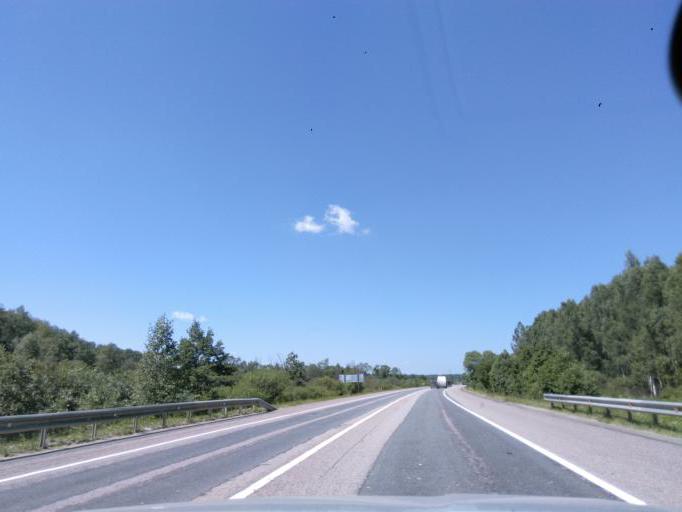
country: RU
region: Moskovskaya
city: Solnechnogorsk
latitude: 56.1457
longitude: 36.9405
